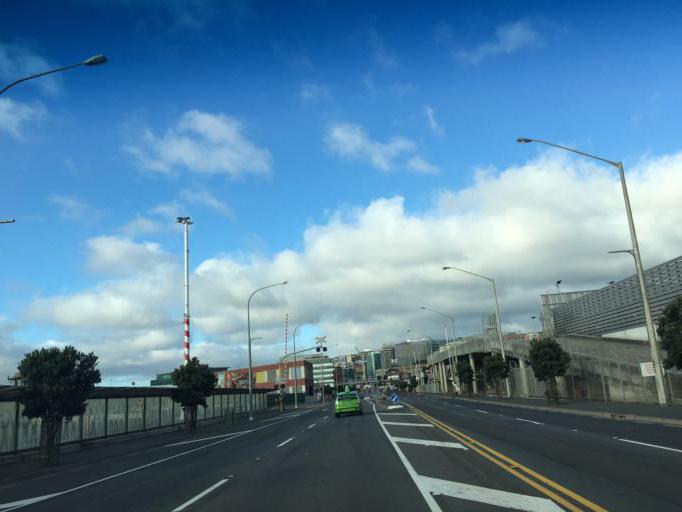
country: NZ
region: Wellington
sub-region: Wellington City
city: Wellington
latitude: -41.2742
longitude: 174.7864
